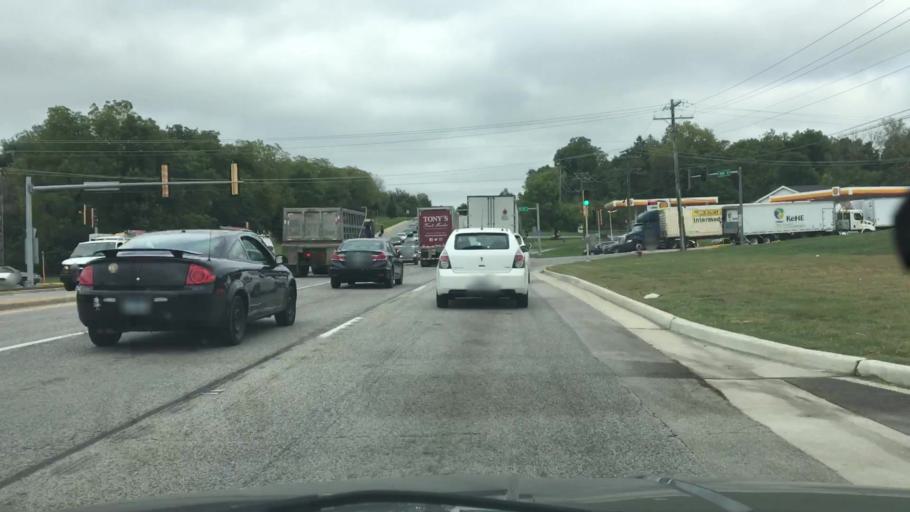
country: US
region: Illinois
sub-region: DuPage County
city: Woodridge
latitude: 41.7498
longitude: -88.0649
